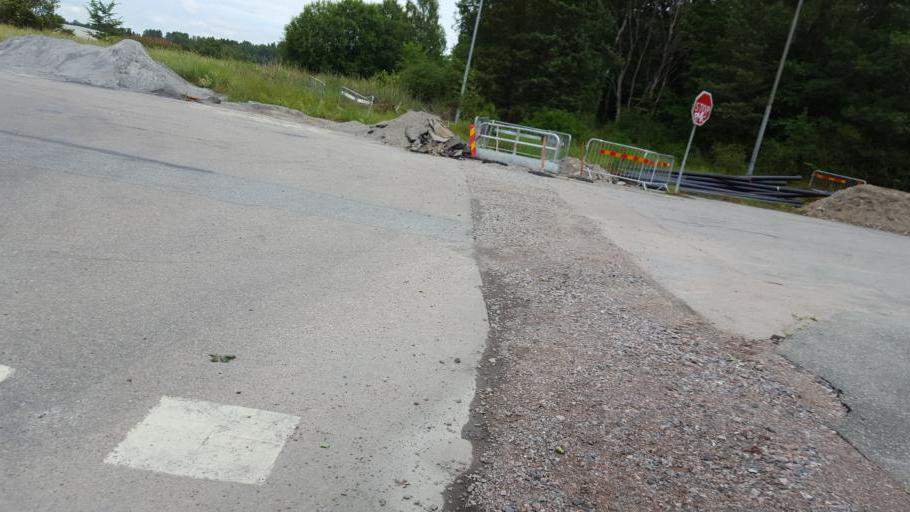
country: SE
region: Stockholm
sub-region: Upplands Vasby Kommun
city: Upplands Vaesby
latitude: 59.5083
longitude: 17.8895
